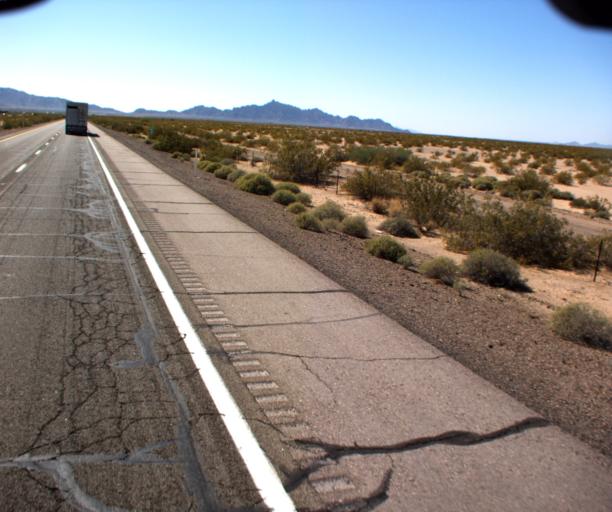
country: US
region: Arizona
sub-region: Yuma County
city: Wellton
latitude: 32.7654
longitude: -113.6238
